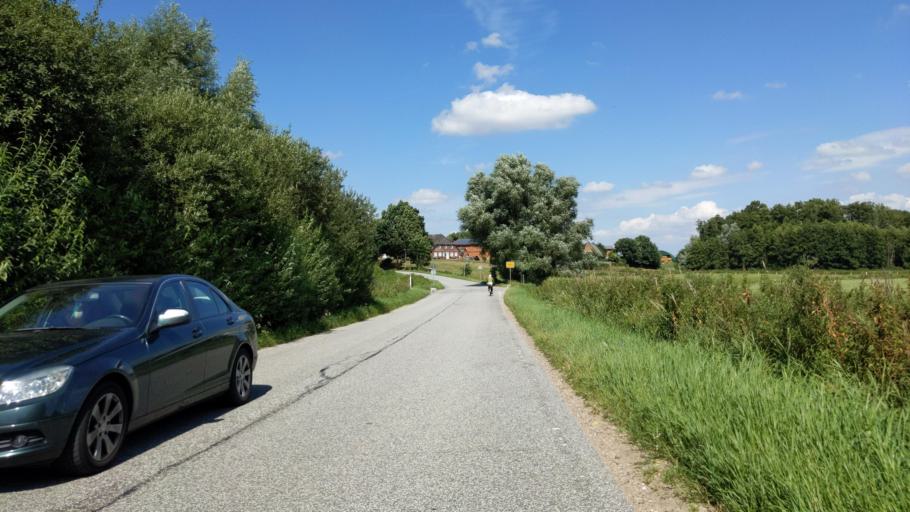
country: DE
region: Schleswig-Holstein
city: Krummesse
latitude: 53.8131
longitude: 10.6798
